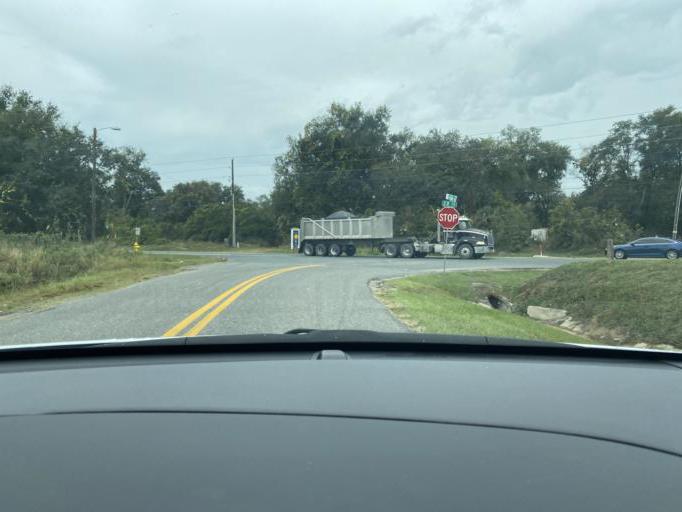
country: US
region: Florida
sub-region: Lake County
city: Groveland
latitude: 28.5874
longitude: -81.8513
